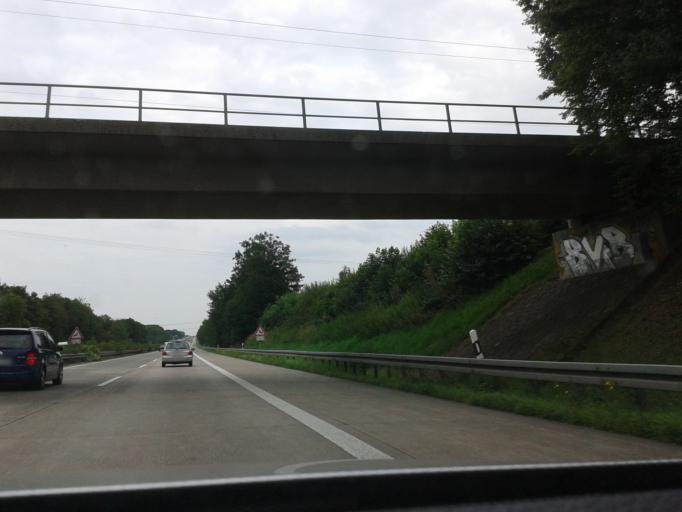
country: DE
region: North Rhine-Westphalia
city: Geseke
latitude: 51.5970
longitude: 8.5170
